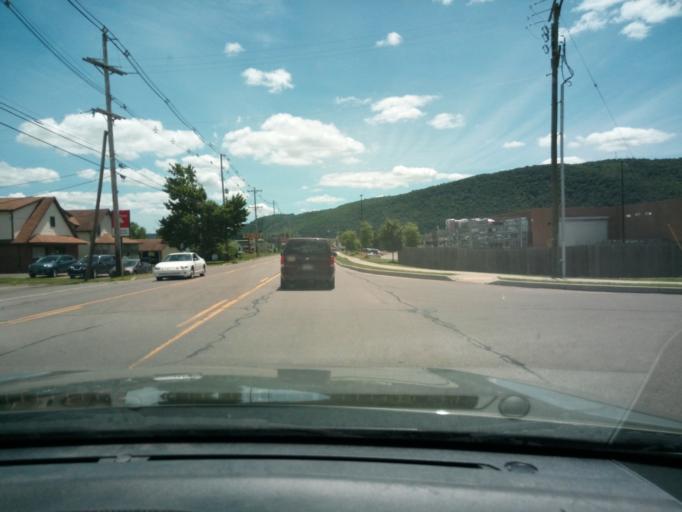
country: US
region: Pennsylvania
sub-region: Bradford County
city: South Waverly
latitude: 41.9780
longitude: -76.5418
